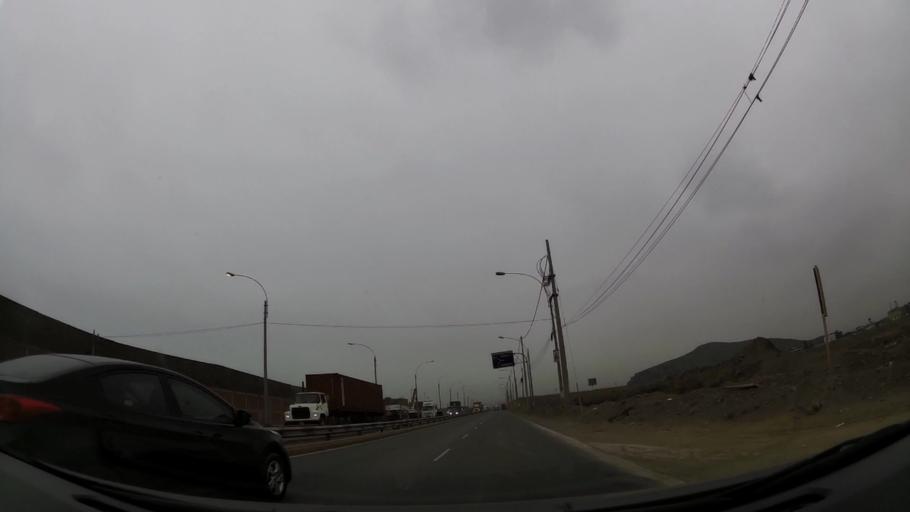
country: PE
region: Callao
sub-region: Callao
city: Callao
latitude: -12.0010
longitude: -77.1267
